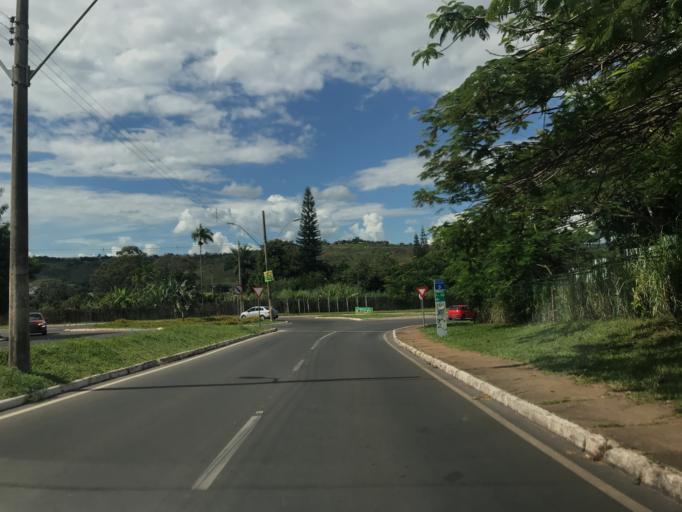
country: BR
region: Federal District
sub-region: Brasilia
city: Brasilia
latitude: -15.7187
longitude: -47.8783
